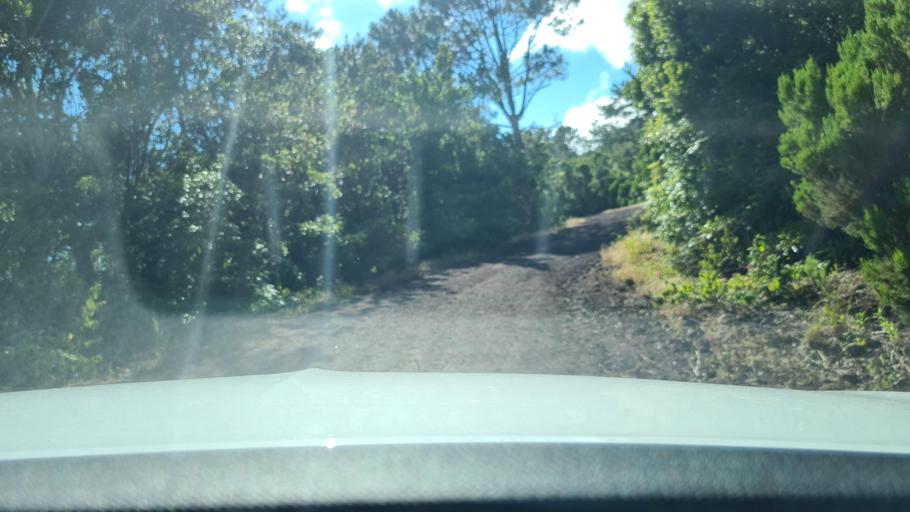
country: PT
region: Azores
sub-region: Sao Roque do Pico
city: Sao Roque do Pico
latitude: 38.4126
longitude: -28.3128
